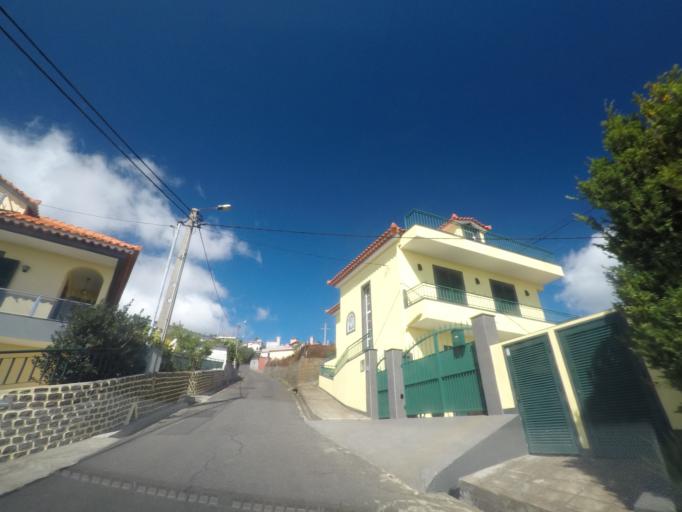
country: PT
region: Madeira
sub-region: Ribeira Brava
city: Campanario
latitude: 32.6922
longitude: -17.0366
